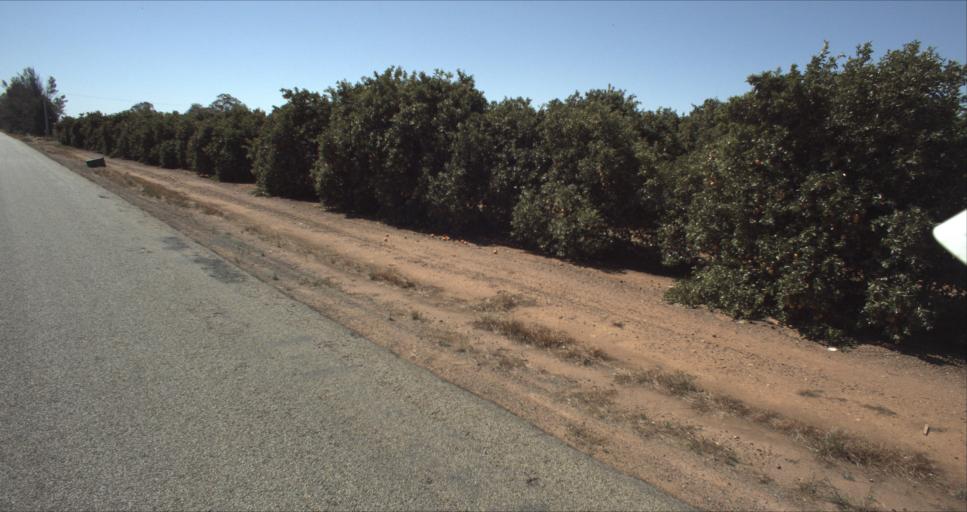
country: AU
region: New South Wales
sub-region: Leeton
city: Leeton
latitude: -34.5372
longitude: 146.3590
